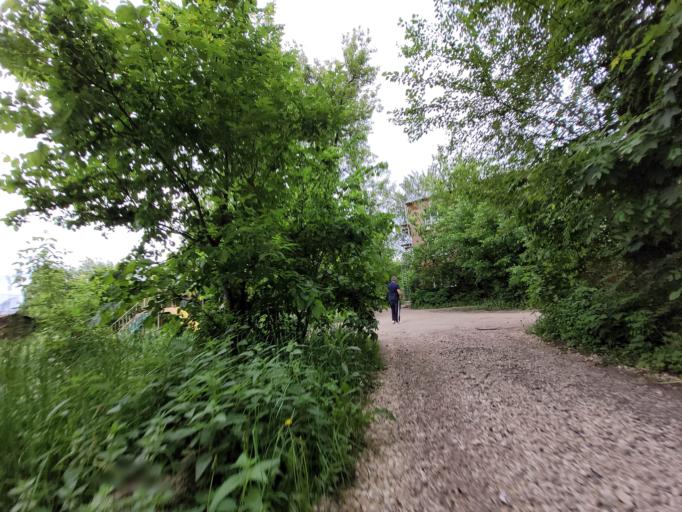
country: RU
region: Moskovskaya
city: Lesnyye Polyany
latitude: 55.9449
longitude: 37.8633
